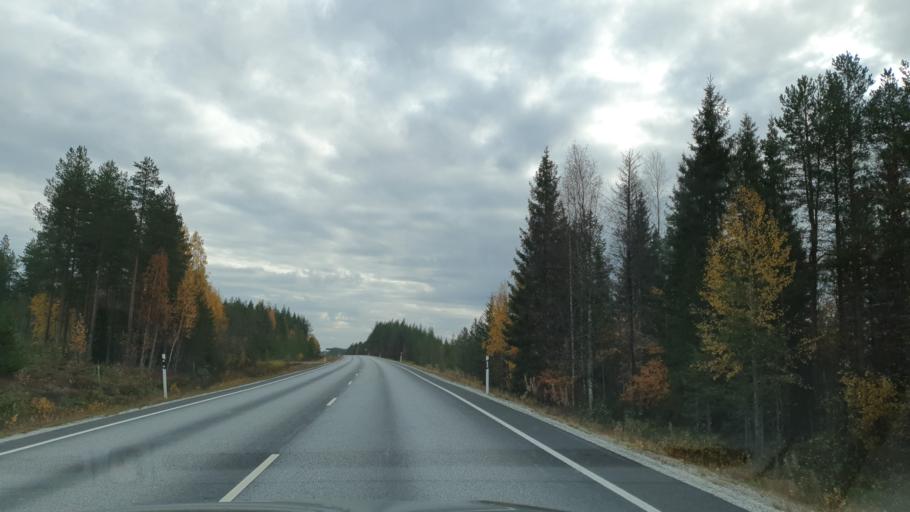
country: FI
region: Northern Ostrobothnia
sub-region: Oulunkaari
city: Pudasjaervi
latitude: 65.4164
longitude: 26.8794
